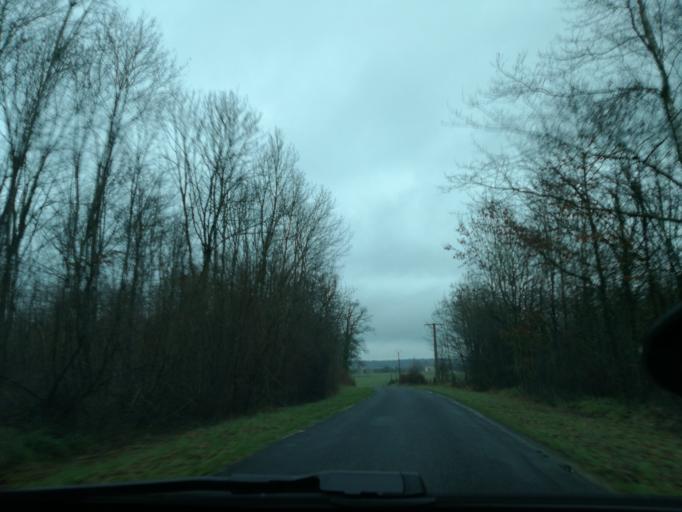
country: FR
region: Lorraine
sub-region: Departement de la Meuse
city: Revigny-sur-Ornain
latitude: 48.8600
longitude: 5.0713
